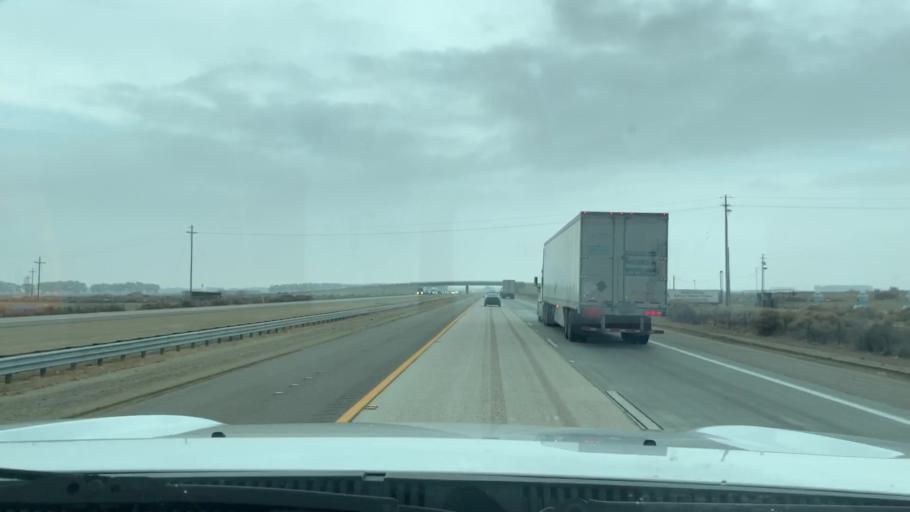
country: US
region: California
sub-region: Kern County
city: Lost Hills
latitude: 35.5556
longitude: -119.5951
